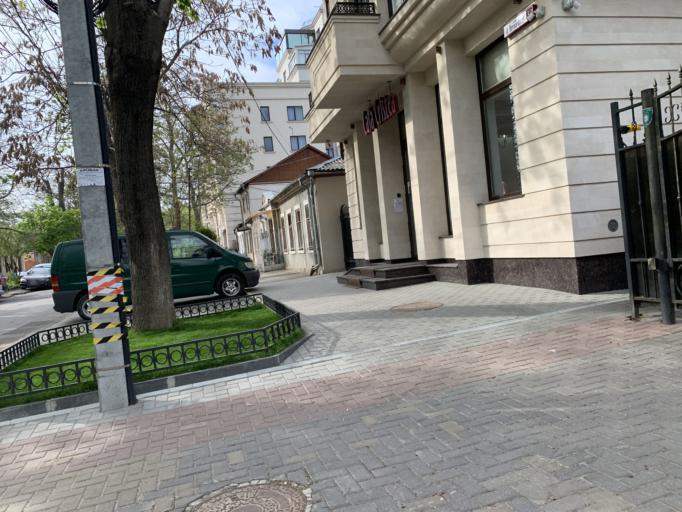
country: MD
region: Chisinau
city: Chisinau
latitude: 47.0133
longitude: 28.8324
